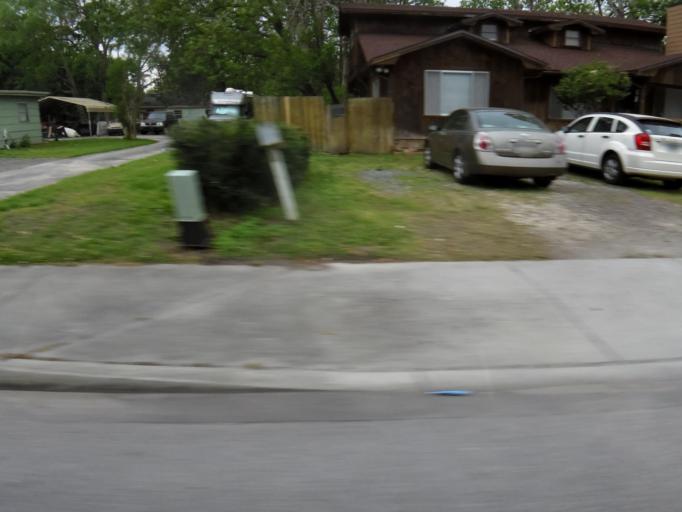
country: US
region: Florida
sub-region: Duval County
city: Jacksonville
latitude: 30.2814
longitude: -81.6183
